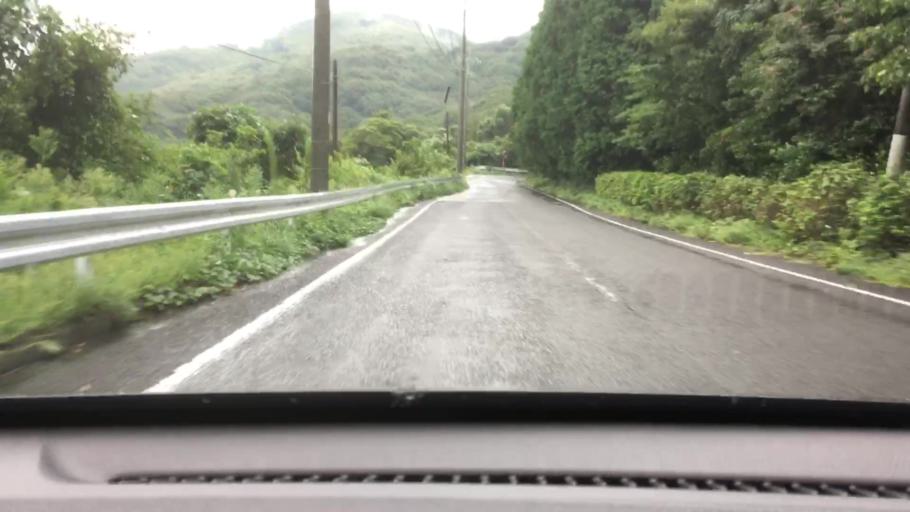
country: JP
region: Nagasaki
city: Togitsu
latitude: 32.8770
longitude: 129.7599
